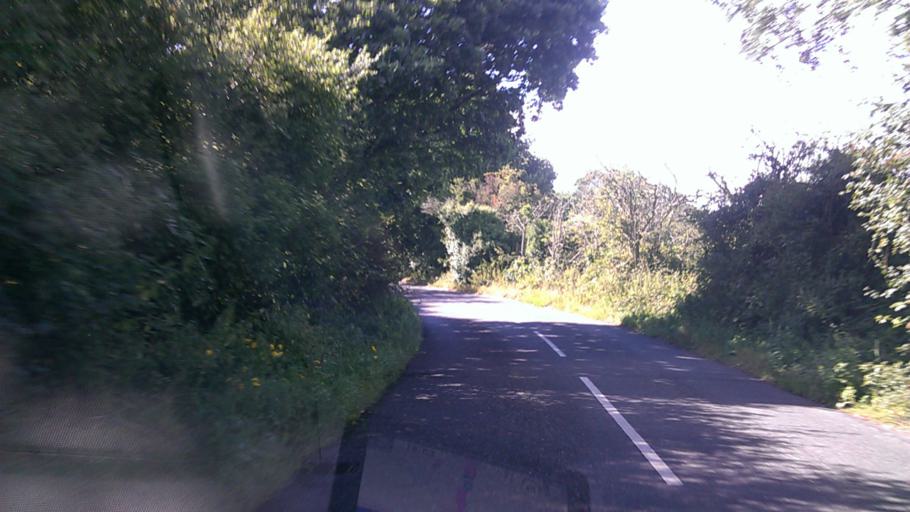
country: GB
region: England
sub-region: Essex
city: Layer de la Haye
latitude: 51.8392
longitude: 0.8997
